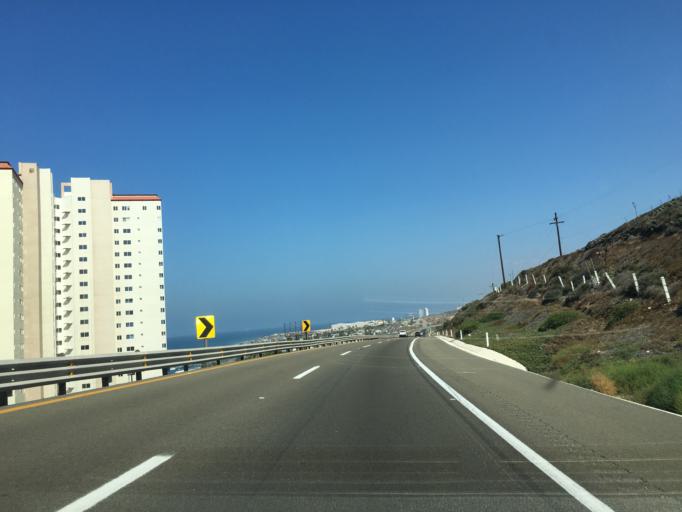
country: MX
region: Baja California
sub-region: Playas de Rosarito
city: Ciudad Morelos
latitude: 32.2716
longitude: -117.0228
